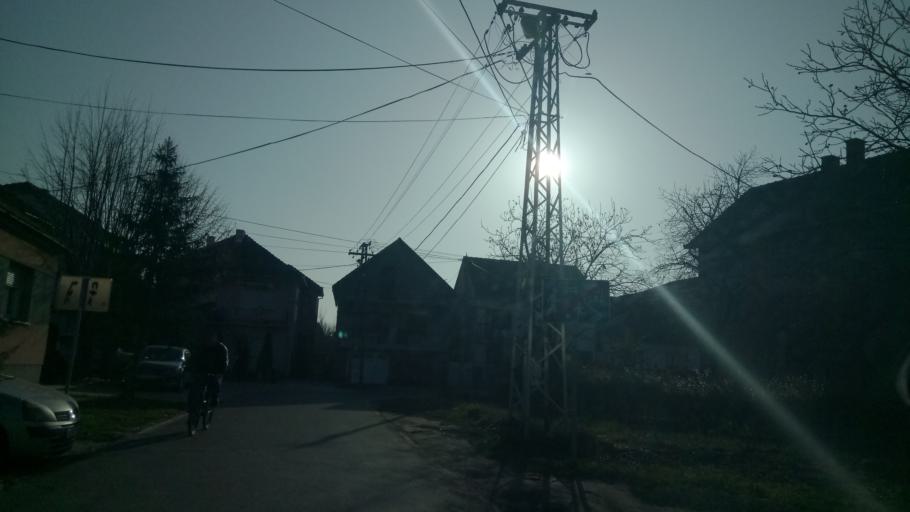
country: RS
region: Autonomna Pokrajina Vojvodina
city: Nova Pazova
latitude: 44.9432
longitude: 20.2146
